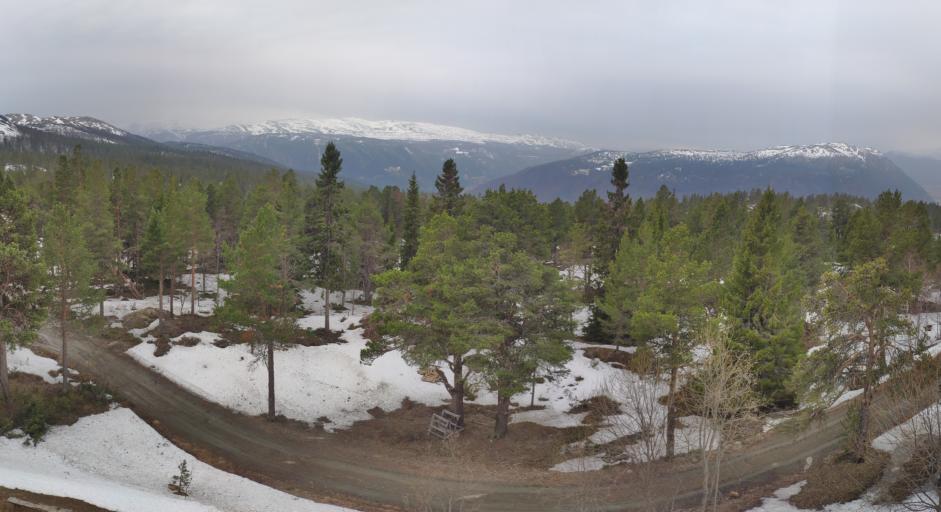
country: NO
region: Oppland
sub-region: Sel
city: Otta
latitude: 61.7923
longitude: 9.5999
